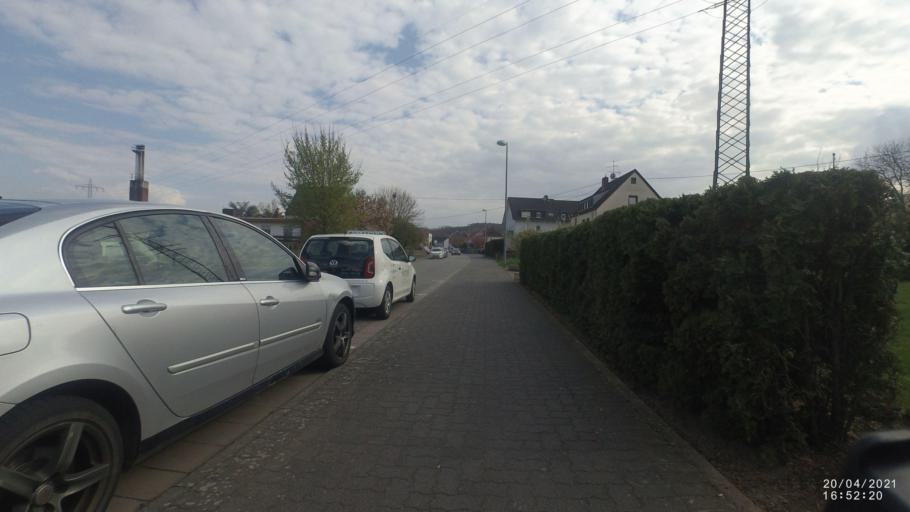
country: DE
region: Rheinland-Pfalz
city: Kettig
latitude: 50.4027
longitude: 7.4617
